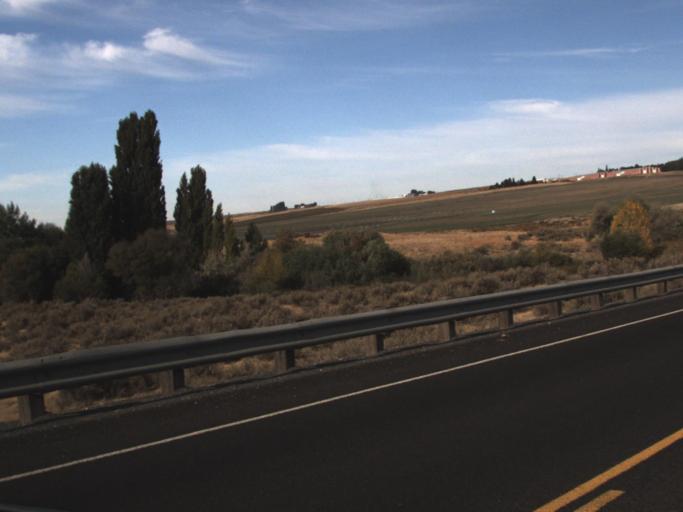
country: US
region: Washington
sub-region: Franklin County
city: Connell
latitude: 46.6569
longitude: -118.8747
